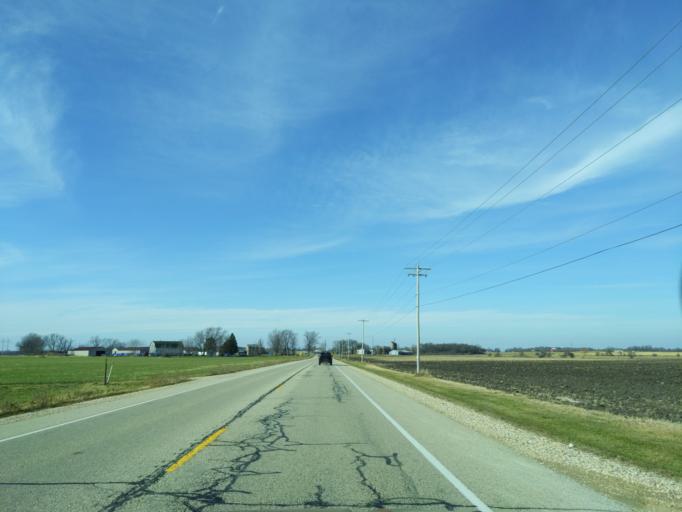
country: US
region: Wisconsin
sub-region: Walworth County
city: Whitewater
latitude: 42.8123
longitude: -88.6849
